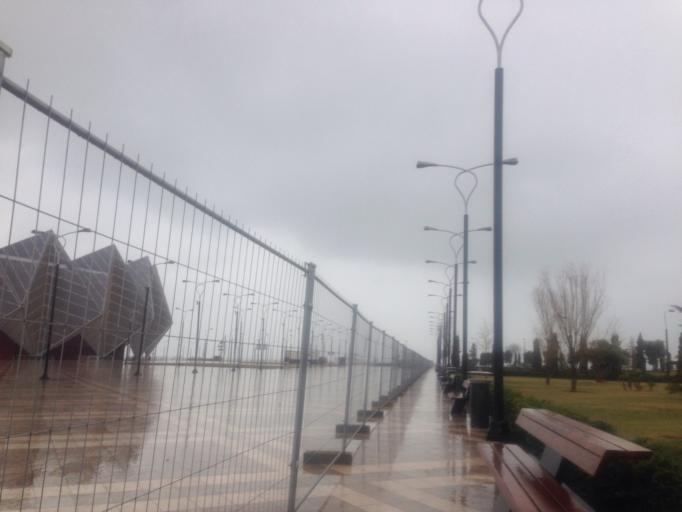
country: AZ
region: Baki
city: Badamdar
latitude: 40.3446
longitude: 49.8477
